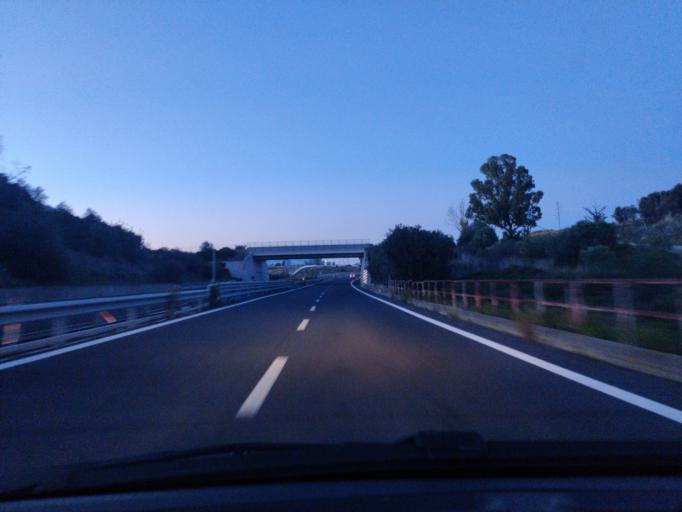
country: IT
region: Latium
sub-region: Citta metropolitana di Roma Capitale
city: Aurelia
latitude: 42.1190
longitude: 11.7915
